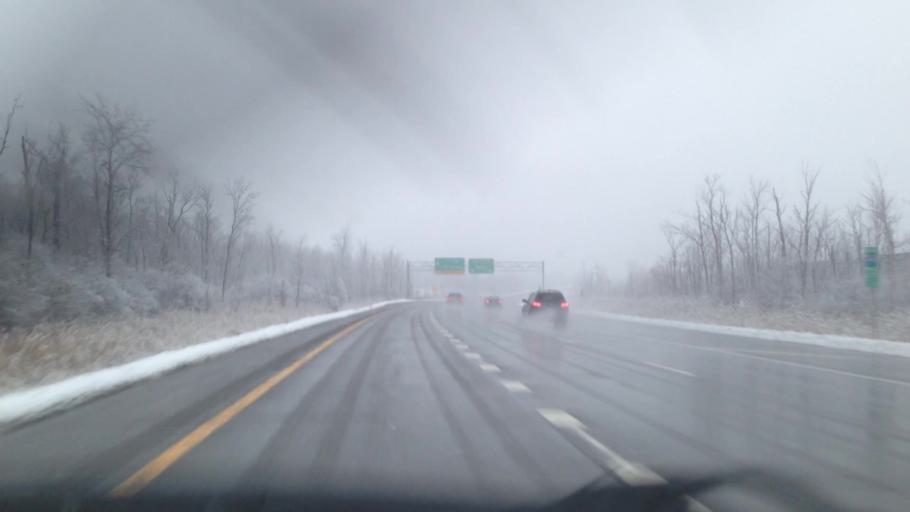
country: US
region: New York
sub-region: Onondaga County
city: East Syracuse
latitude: 43.0561
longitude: -76.0611
